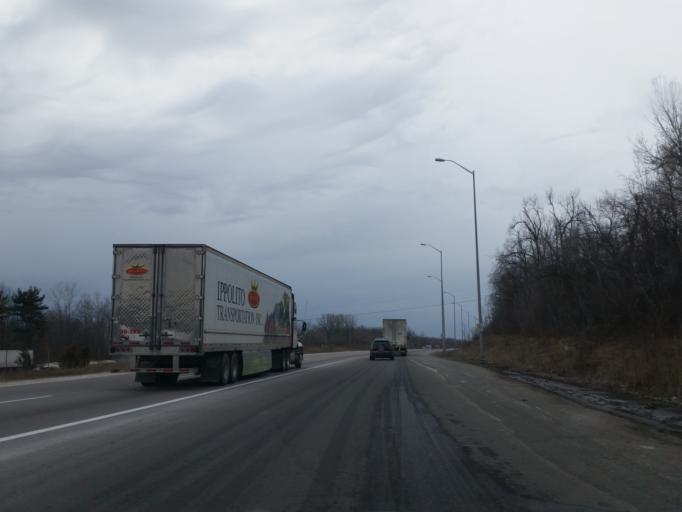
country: CA
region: Ontario
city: Quinte West
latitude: 44.1097
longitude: -77.6612
